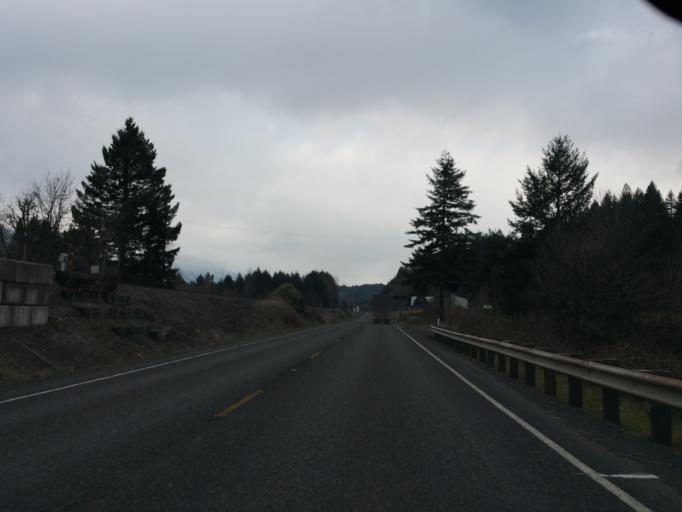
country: US
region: Washington
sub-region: Skamania County
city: Stevenson
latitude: 45.6850
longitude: -121.8968
